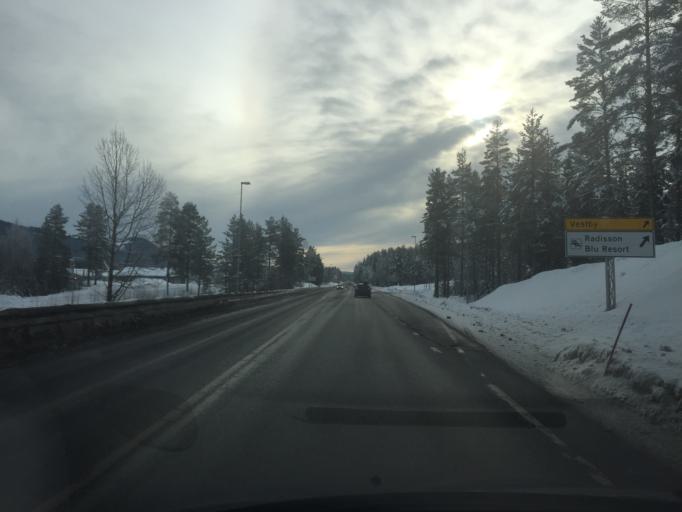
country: NO
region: Hedmark
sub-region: Trysil
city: Innbygda
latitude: 61.2983
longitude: 12.2654
